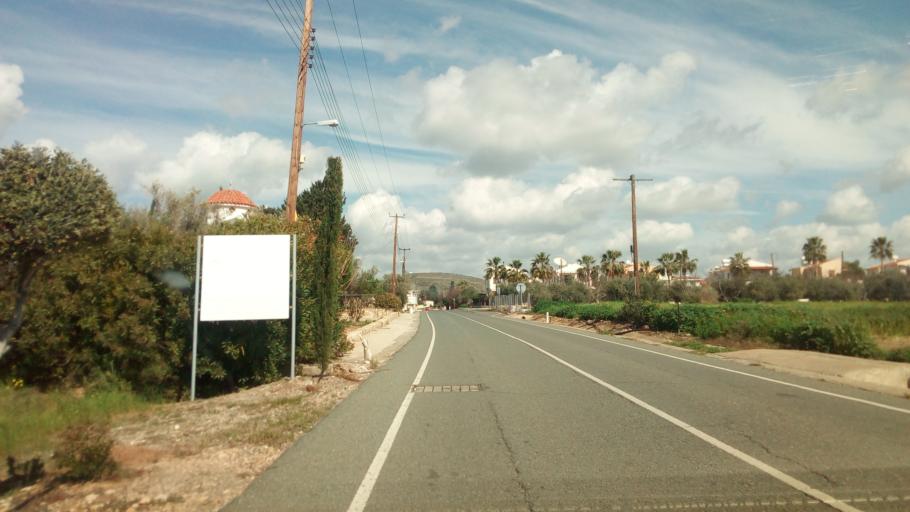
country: CY
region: Pafos
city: Mesogi
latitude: 34.7349
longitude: 32.5332
